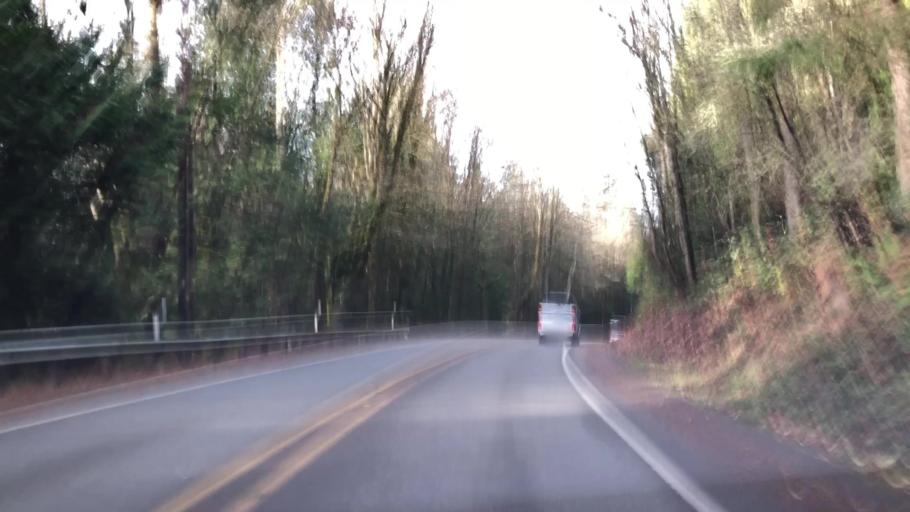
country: US
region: Washington
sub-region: Kitsap County
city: Indianola
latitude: 47.7521
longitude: -122.5446
